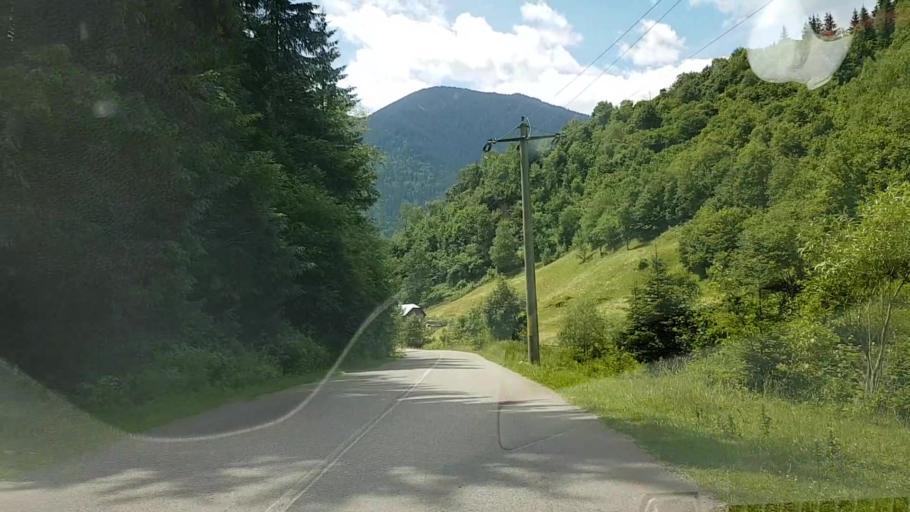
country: RO
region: Suceava
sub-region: Comuna Crucea
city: Crucea
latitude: 47.4064
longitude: 25.5760
